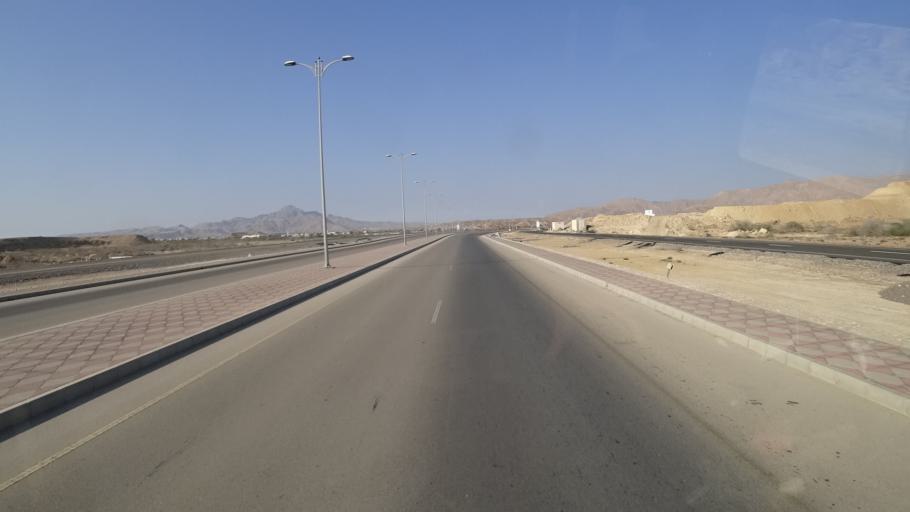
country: OM
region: Ash Sharqiyah
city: Sur
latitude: 22.5853
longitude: 59.4753
